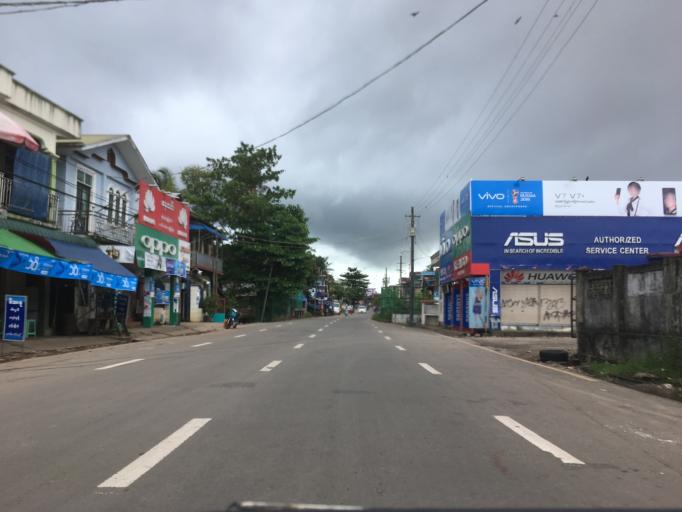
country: MM
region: Mon
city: Mawlamyine
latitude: 16.4648
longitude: 97.6240
